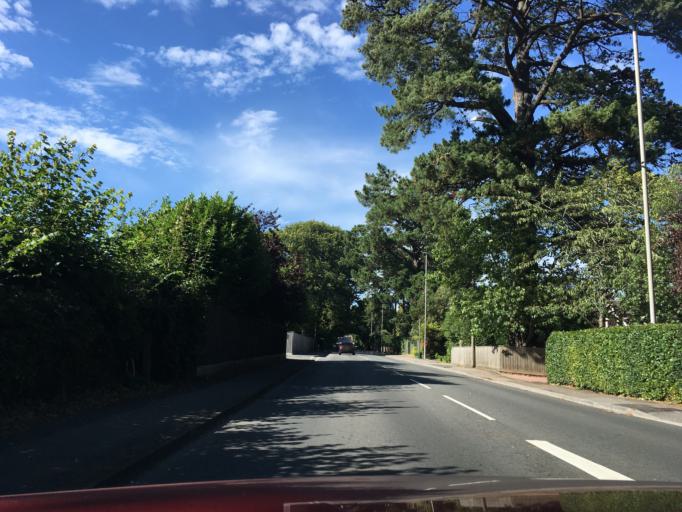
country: GB
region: England
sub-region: Dorset
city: Ferndown
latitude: 50.7829
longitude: -1.8815
